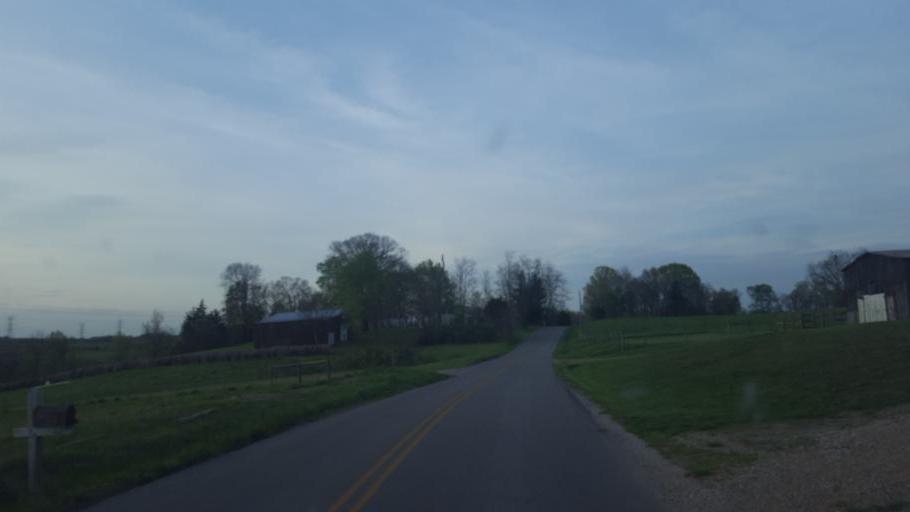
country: US
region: Kentucky
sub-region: Metcalfe County
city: Edmonton
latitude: 37.0519
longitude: -85.7052
